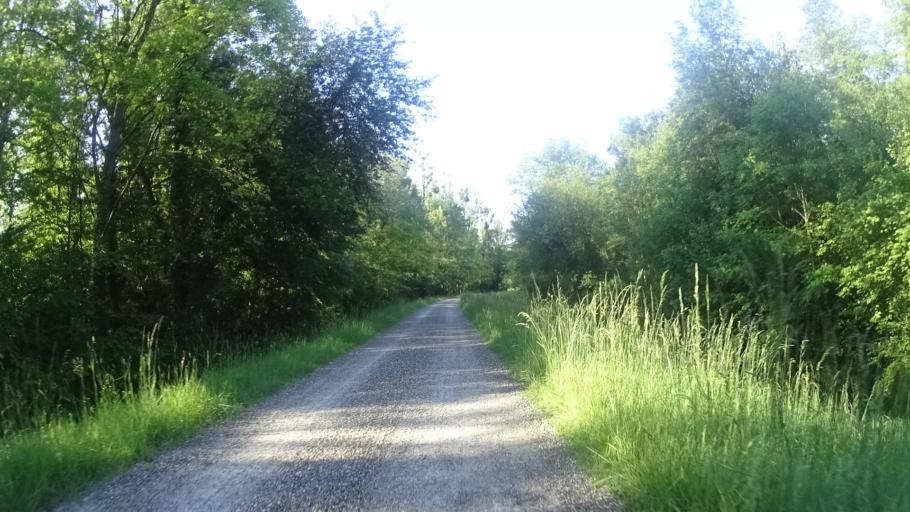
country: DE
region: Baden-Wuerttemberg
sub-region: Freiburg Region
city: Rheinau
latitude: 48.6931
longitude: 7.9512
